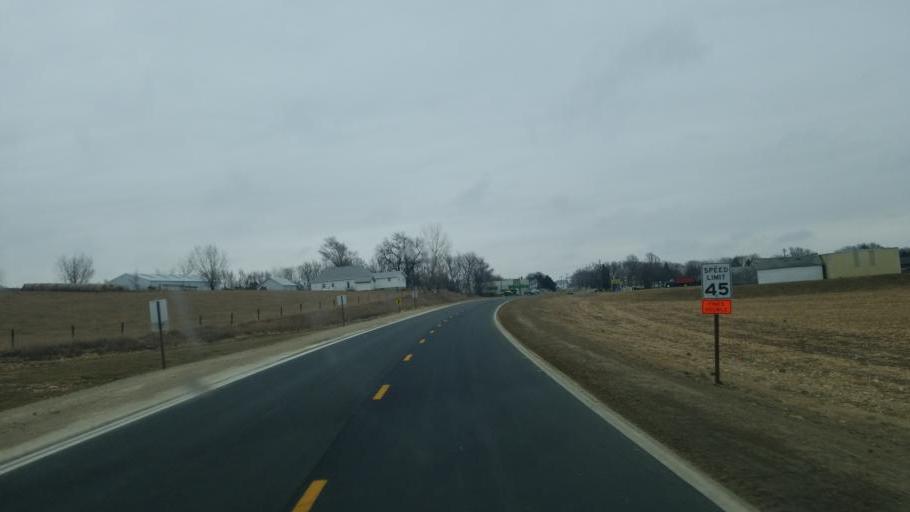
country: US
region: Nebraska
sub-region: Knox County
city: Bloomfield
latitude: 42.5995
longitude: -97.6601
